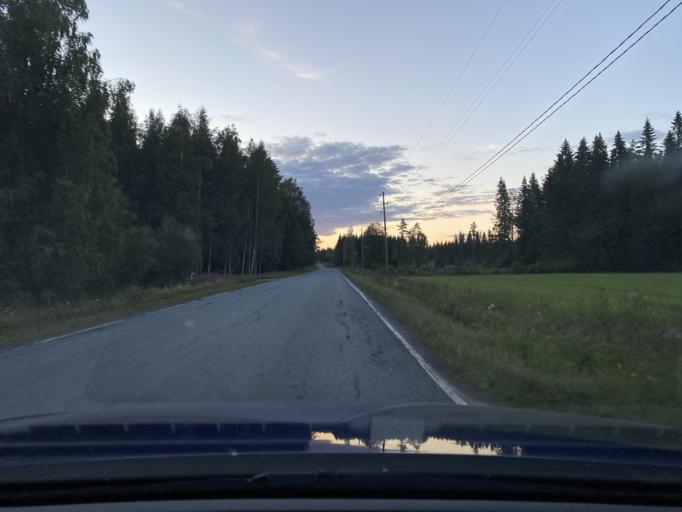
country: FI
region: Haeme
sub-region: Forssa
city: Tammela
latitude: 60.8805
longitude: 23.9219
